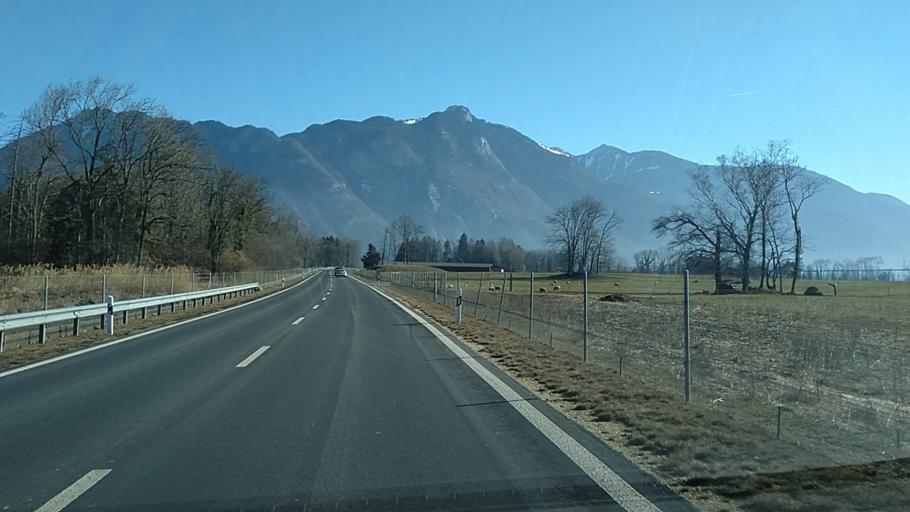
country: CH
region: Valais
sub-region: Monthey District
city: Vouvry
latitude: 46.3573
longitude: 6.8890
